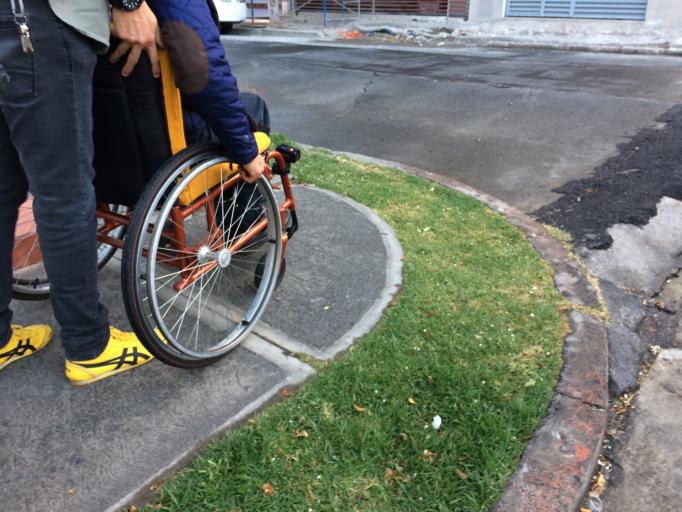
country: MX
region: Michoacan
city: Morelia
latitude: 19.6927
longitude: -101.1784
